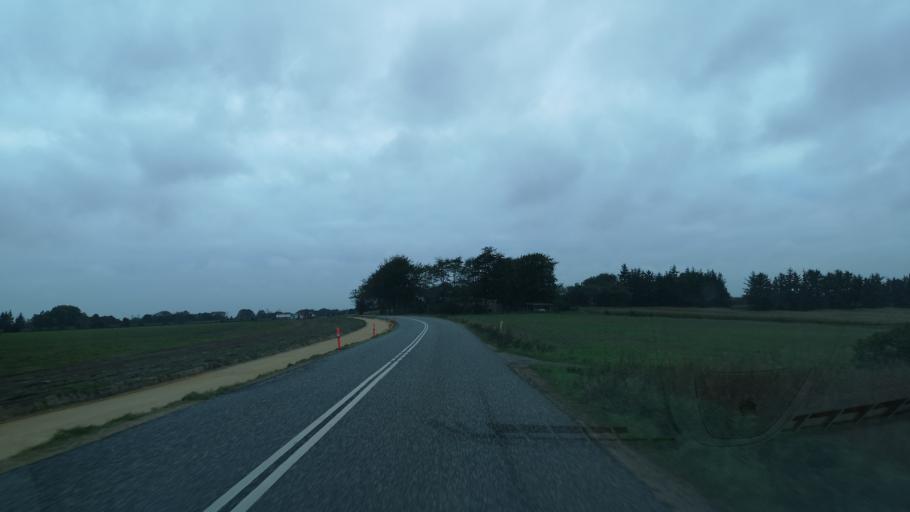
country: DK
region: Central Jutland
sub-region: Ringkobing-Skjern Kommune
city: Videbaek
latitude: 56.0547
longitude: 8.6361
